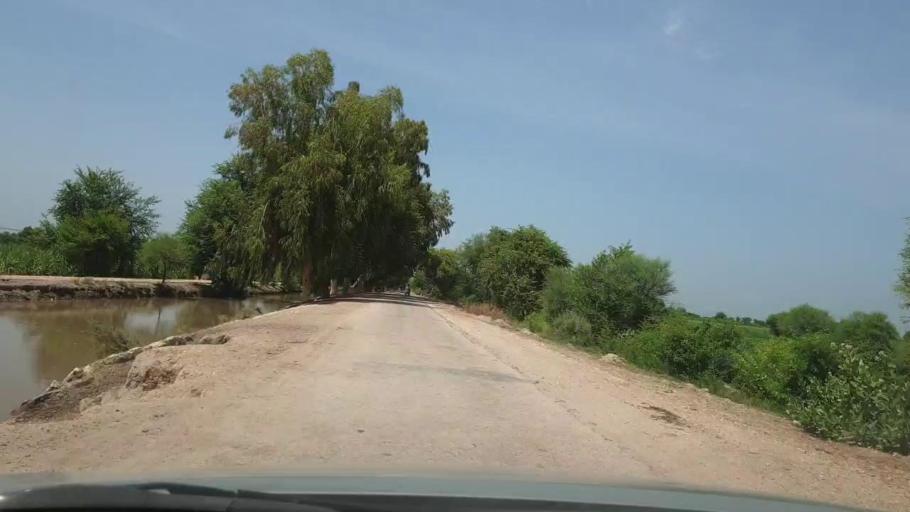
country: PK
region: Sindh
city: Pano Aqil
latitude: 27.6970
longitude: 69.1114
